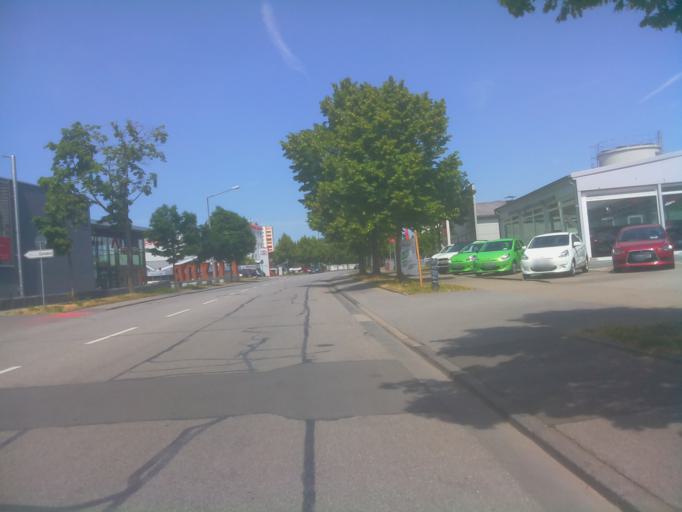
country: DE
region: Hesse
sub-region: Regierungsbezirk Darmstadt
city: Bensheim
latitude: 49.6705
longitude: 8.6070
